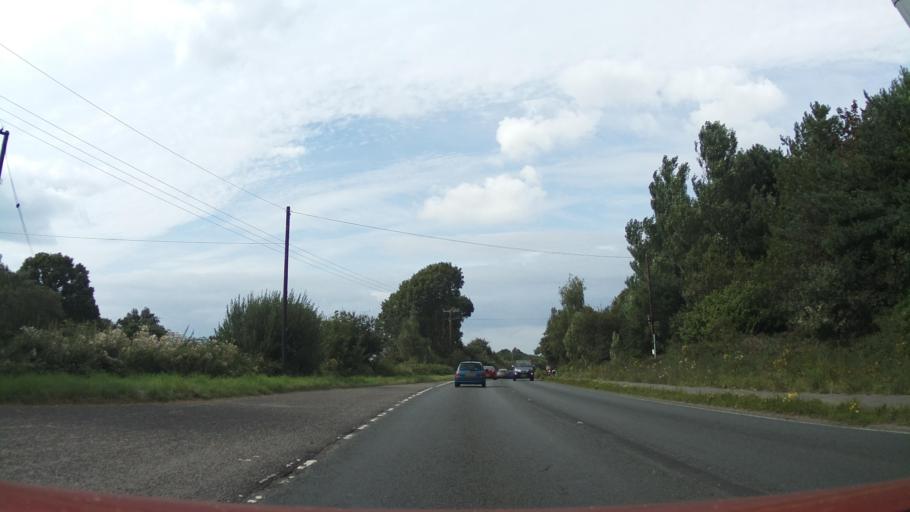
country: GB
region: England
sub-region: Hampshire
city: Marchwood
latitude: 50.8671
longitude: -1.4382
